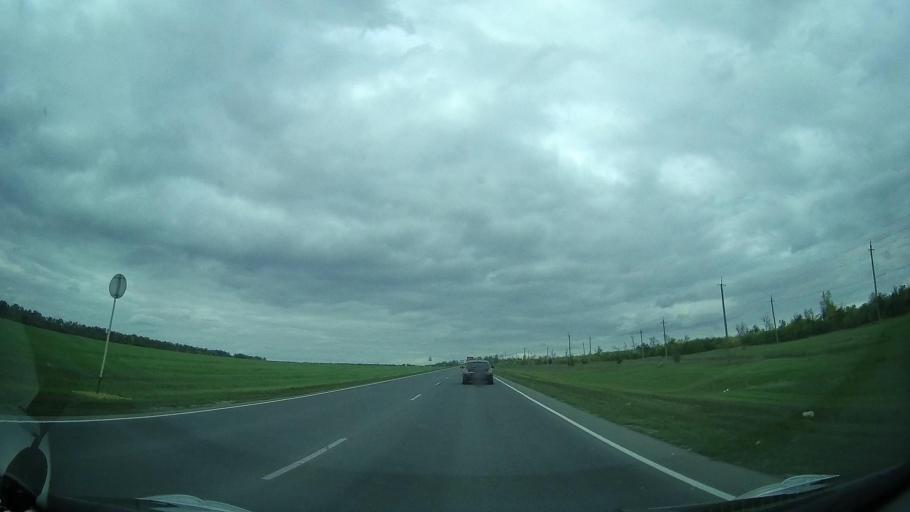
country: RU
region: Rostov
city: Yegorlykskaya
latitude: 46.5707
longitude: 40.6307
